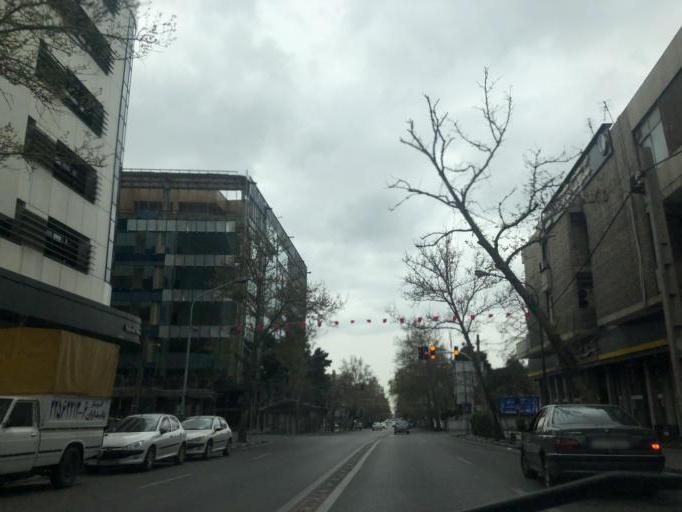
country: IR
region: Tehran
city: Tajrish
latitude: 35.7740
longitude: 51.4631
